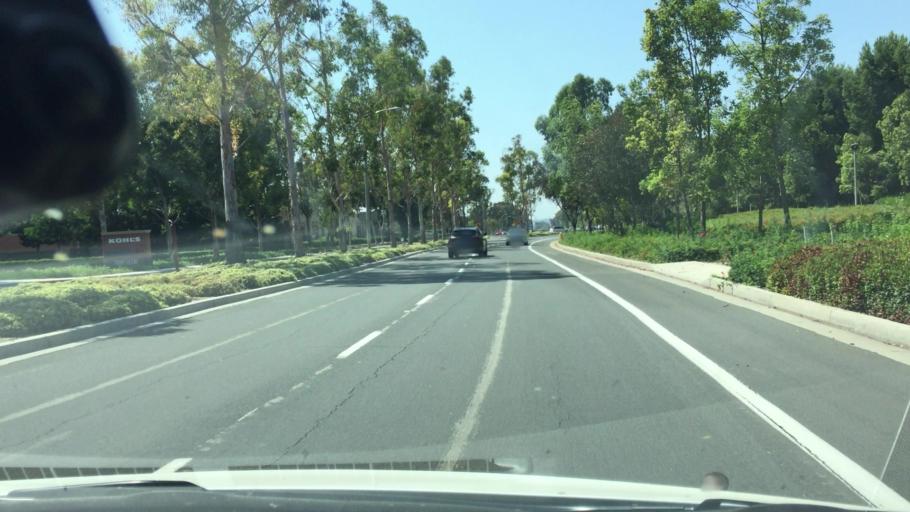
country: US
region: California
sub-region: Orange County
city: Irvine
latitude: 33.6970
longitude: -117.7627
